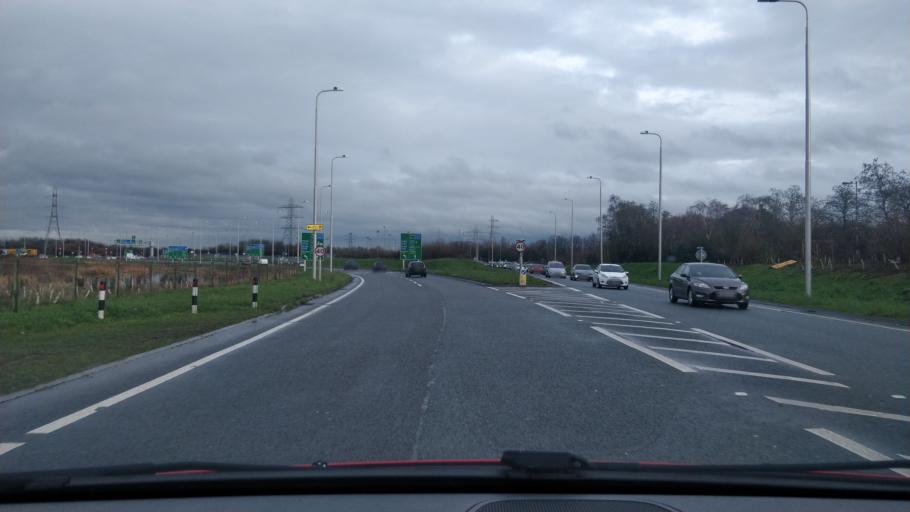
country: GB
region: England
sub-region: Sefton
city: Maghull
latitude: 53.4943
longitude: -2.9586
